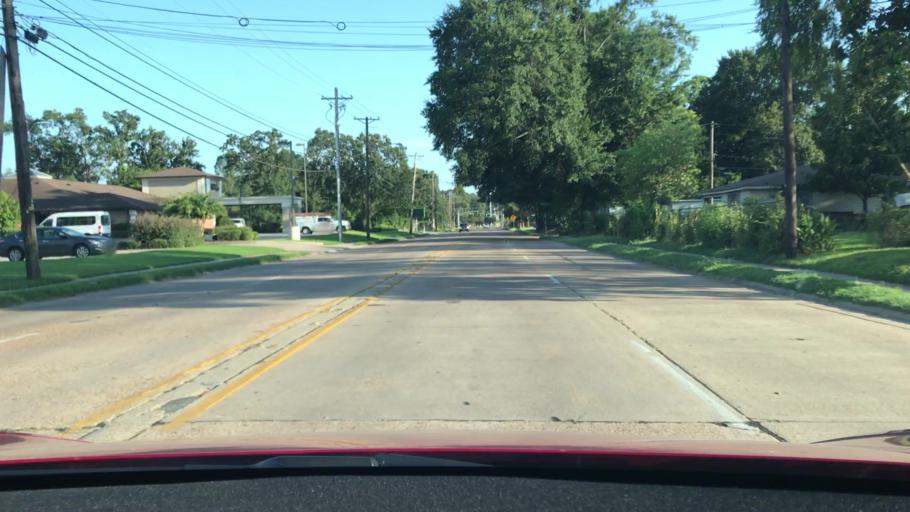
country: US
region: Louisiana
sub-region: Bossier Parish
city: Bossier City
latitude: 32.4362
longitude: -93.7460
